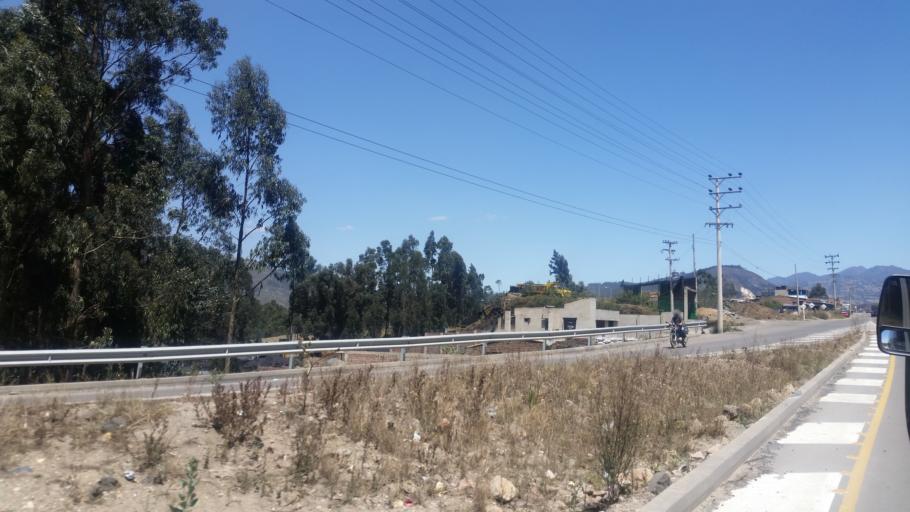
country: CO
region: Boyaca
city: Mongui
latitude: 5.7599
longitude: -72.8871
